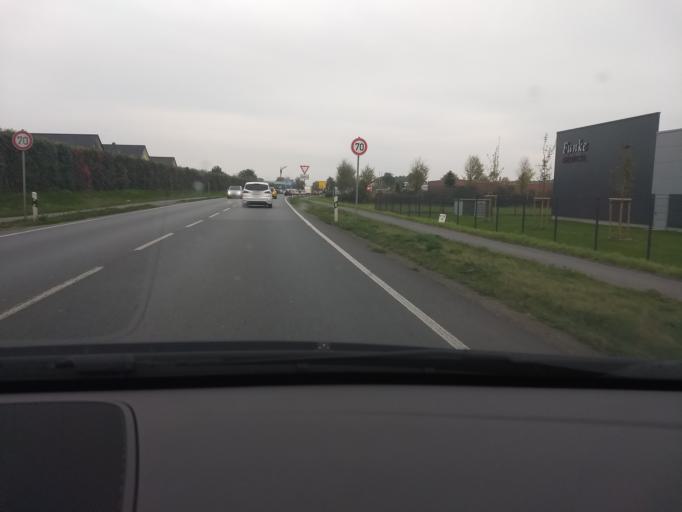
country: DE
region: North Rhine-Westphalia
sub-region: Regierungsbezirk Munster
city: Raesfeld
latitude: 51.7643
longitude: 6.8510
